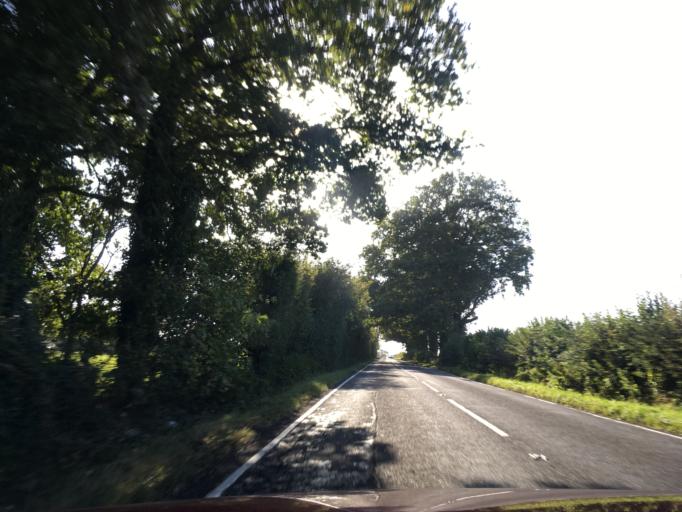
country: GB
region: England
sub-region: Hampshire
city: Four Marks
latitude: 51.0454
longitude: -1.0559
